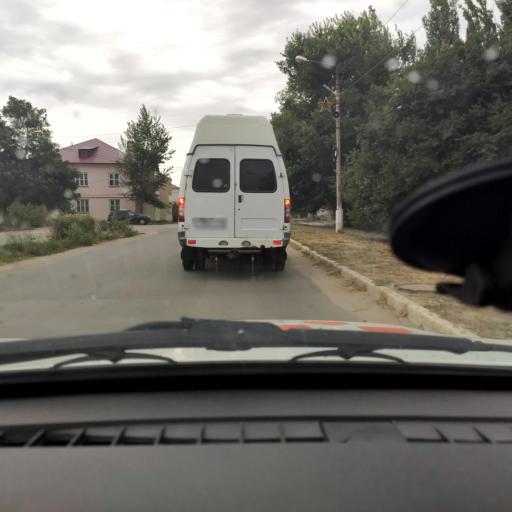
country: RU
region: Voronezj
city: Strelitsa
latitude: 51.6127
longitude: 38.9010
